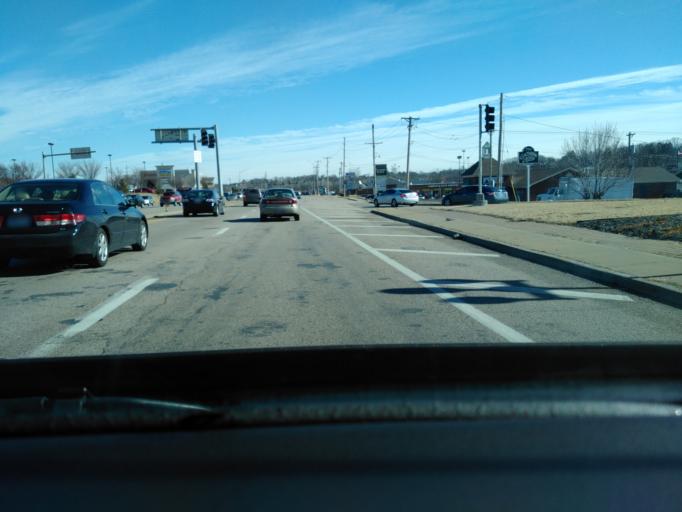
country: US
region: Missouri
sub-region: Saint Louis County
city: Manchester
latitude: 38.5927
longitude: -90.5083
